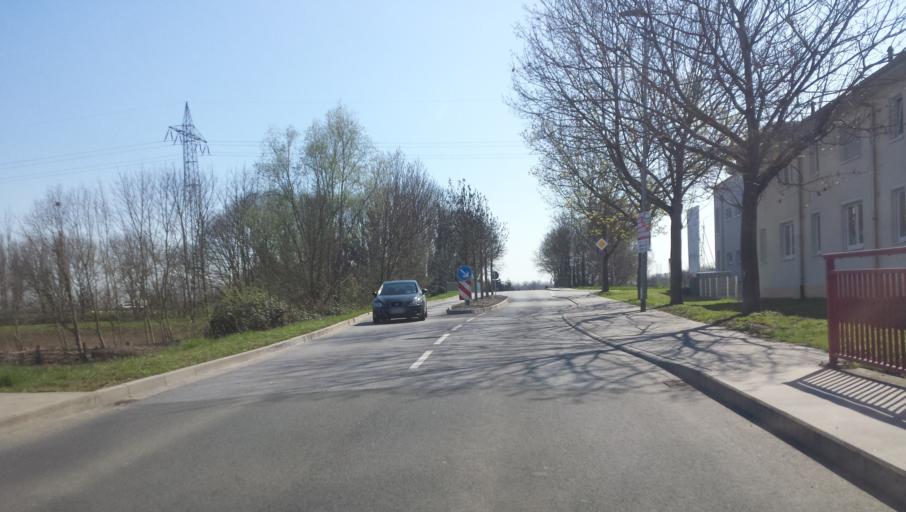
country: DE
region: Hesse
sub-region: Regierungsbezirk Darmstadt
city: Biblis
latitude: 49.6818
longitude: 8.4517
